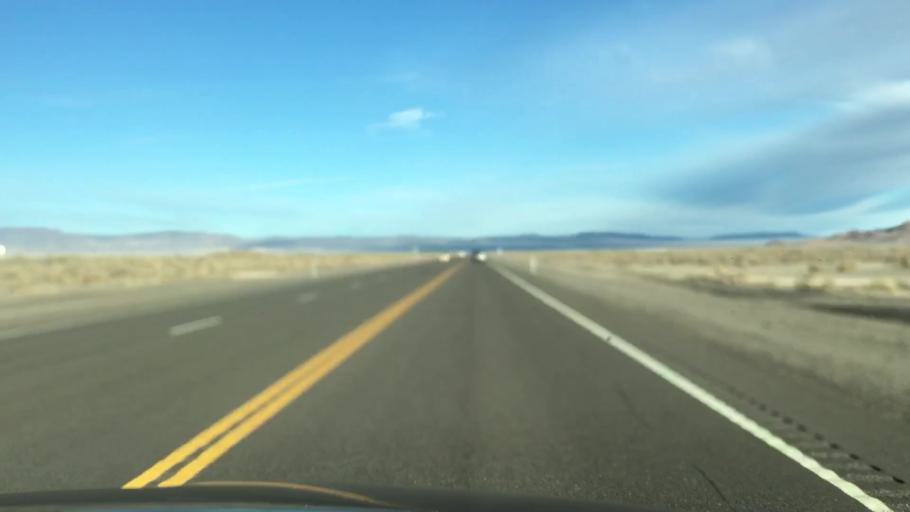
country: US
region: Nevada
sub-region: Nye County
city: Tonopah
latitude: 38.1321
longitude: -117.5440
